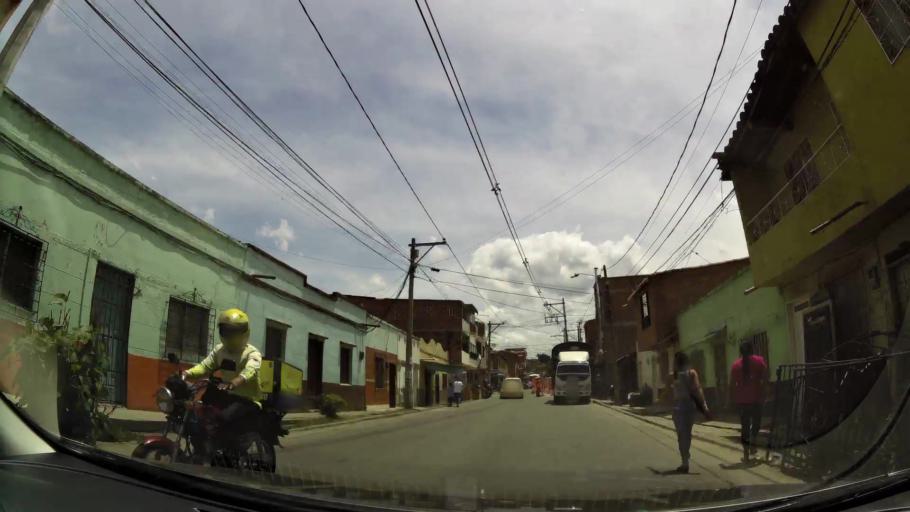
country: CO
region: Antioquia
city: Bello
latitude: 6.3489
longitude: -75.5644
